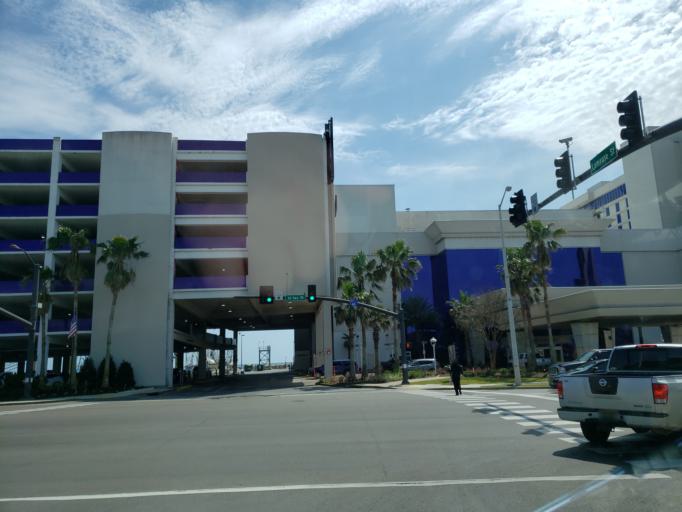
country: US
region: Mississippi
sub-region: Harrison County
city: Biloxi
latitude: 30.3930
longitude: -88.8871
